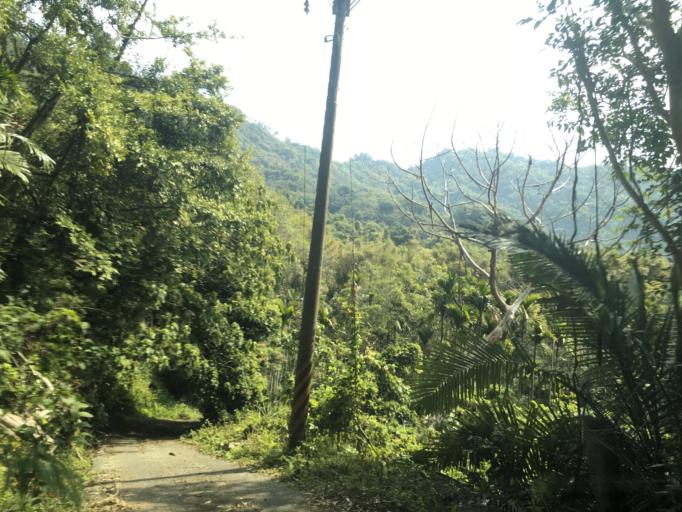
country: TW
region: Taiwan
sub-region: Taichung City
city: Taichung
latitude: 24.1350
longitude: 120.8223
